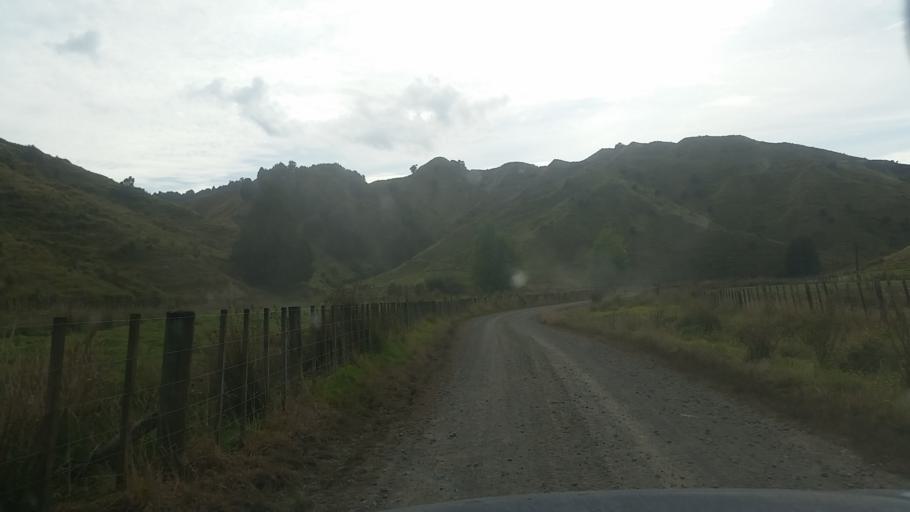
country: NZ
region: Taranaki
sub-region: New Plymouth District
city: Waitara
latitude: -39.1281
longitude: 174.6948
